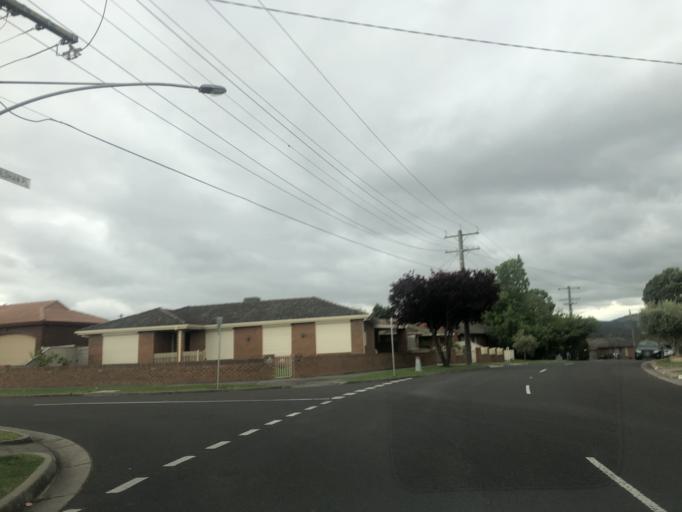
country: AU
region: Victoria
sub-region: Greater Dandenong
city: Dandenong North
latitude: -37.9642
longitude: 145.2205
